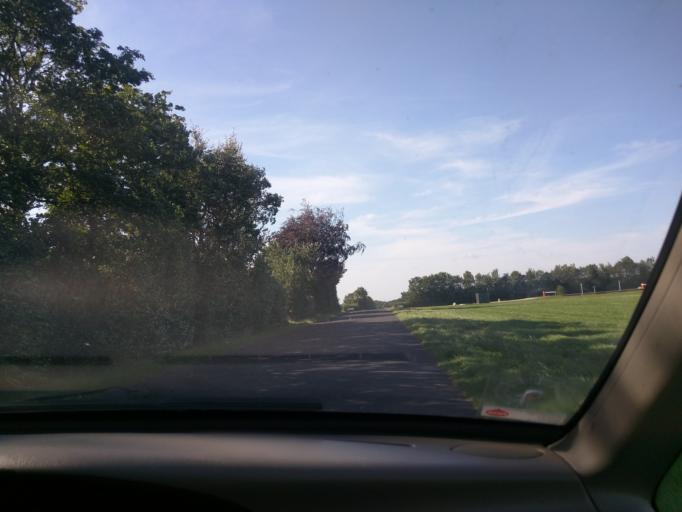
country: DK
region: Central Jutland
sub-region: Viborg Kommune
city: Bjerringbro
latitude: 56.4900
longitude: 9.5925
